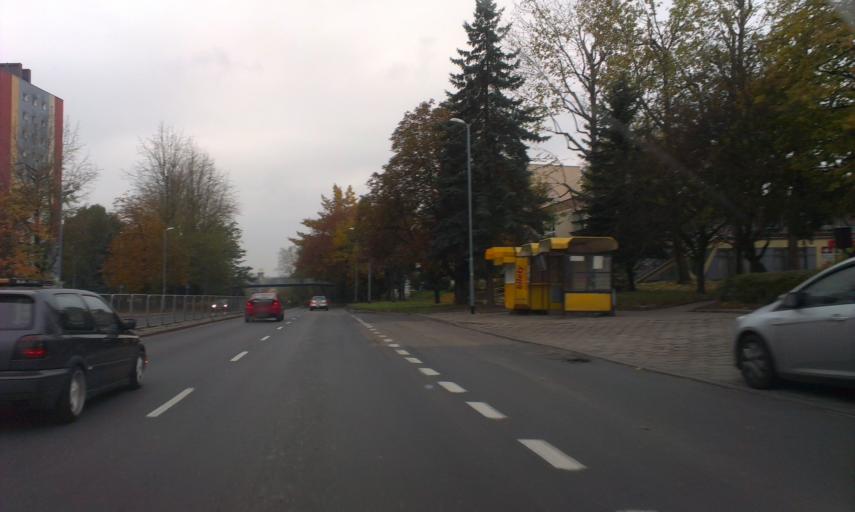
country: PL
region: West Pomeranian Voivodeship
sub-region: Koszalin
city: Koszalin
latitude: 54.1986
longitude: 16.1848
